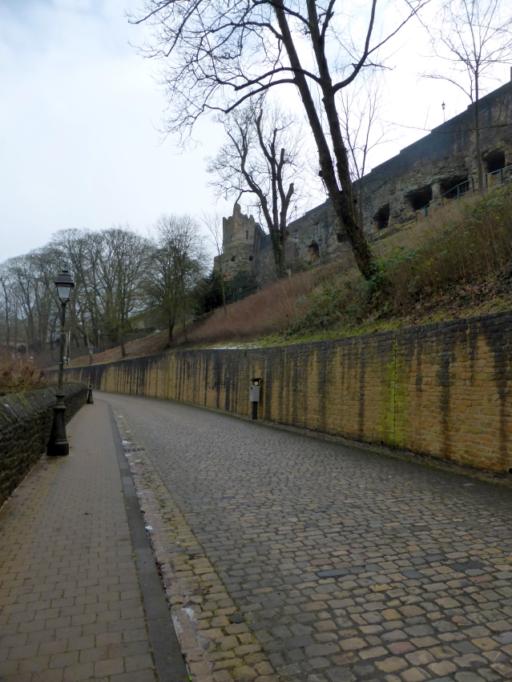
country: LU
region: Luxembourg
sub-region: Canton de Luxembourg
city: Luxembourg
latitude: 49.6121
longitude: 6.1366
